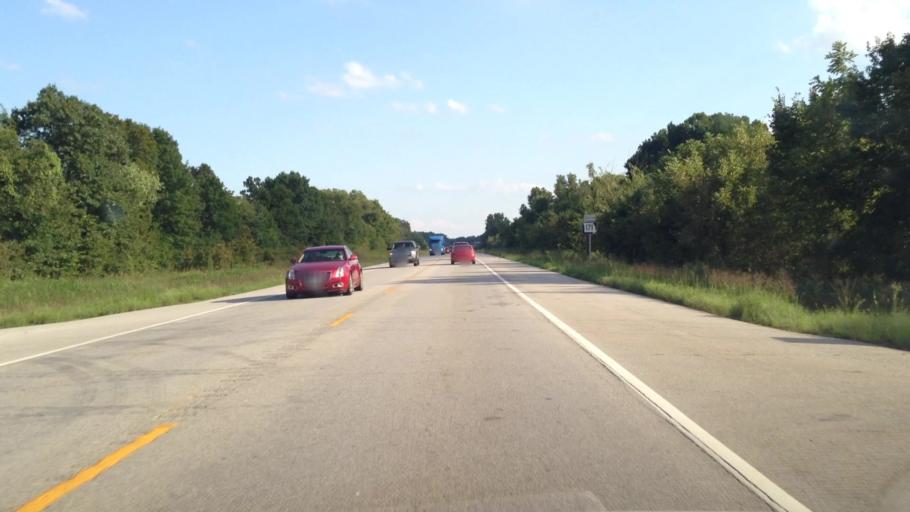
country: US
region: Missouri
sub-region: Jasper County
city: Carl Junction
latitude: 37.1577
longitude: -94.5284
